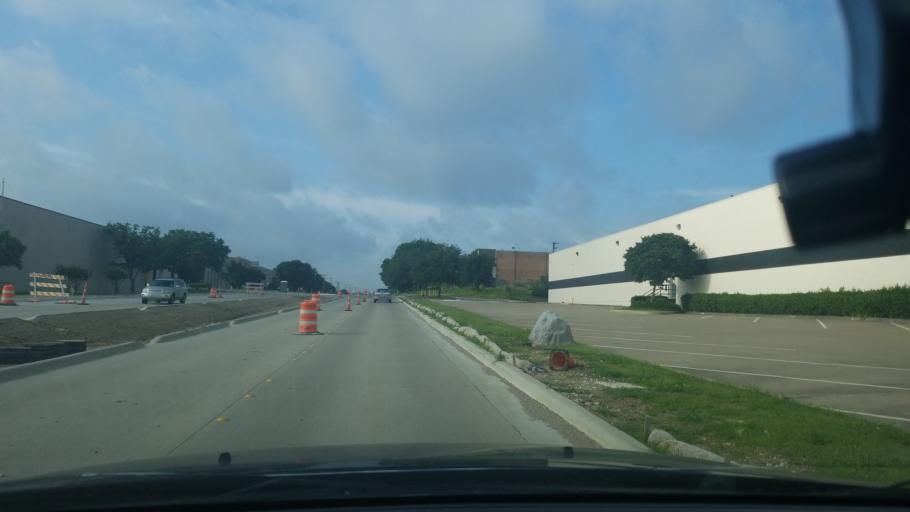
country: US
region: Texas
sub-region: Dallas County
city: Mesquite
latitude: 32.7742
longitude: -96.6468
